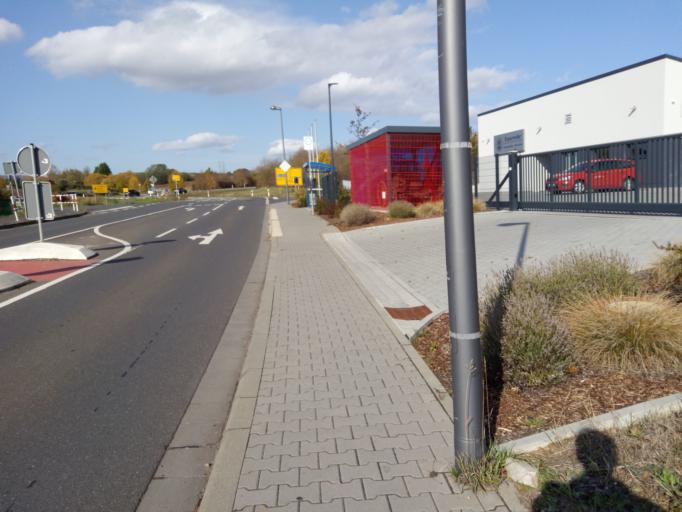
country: DE
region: Rheinland-Pfalz
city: Roxheim
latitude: 49.8681
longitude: 7.8196
